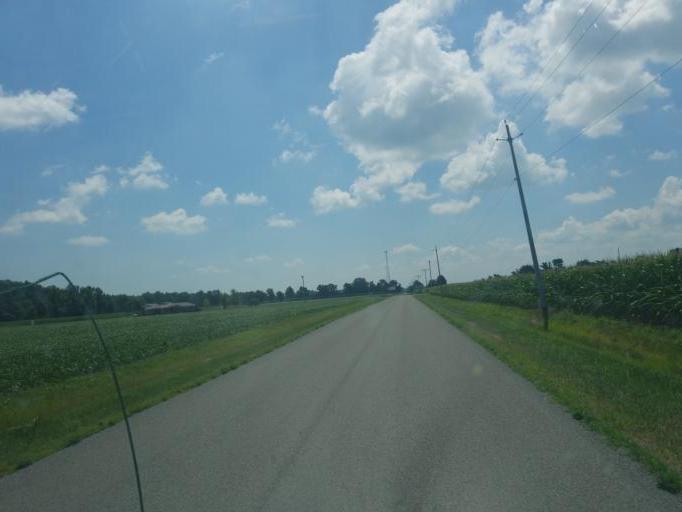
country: US
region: Ohio
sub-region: Mercer County
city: Celina
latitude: 40.5841
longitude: -84.4939
